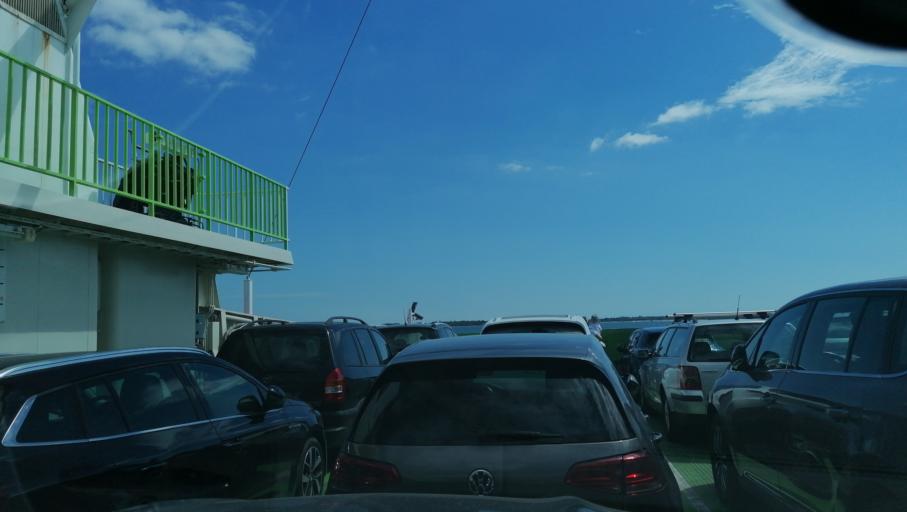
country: PT
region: Setubal
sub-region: Setubal
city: Setubal
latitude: 38.5108
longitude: -8.8853
